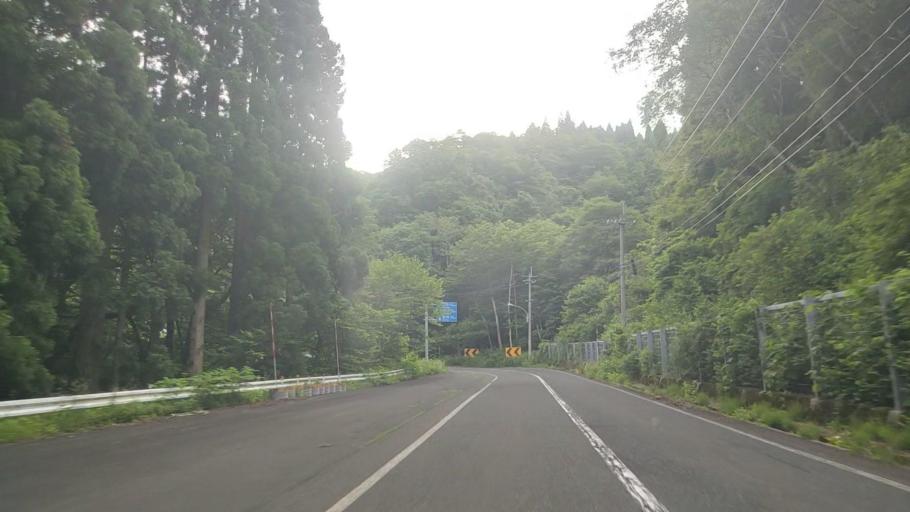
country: JP
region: Tottori
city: Kurayoshi
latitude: 35.3159
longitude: 134.0044
